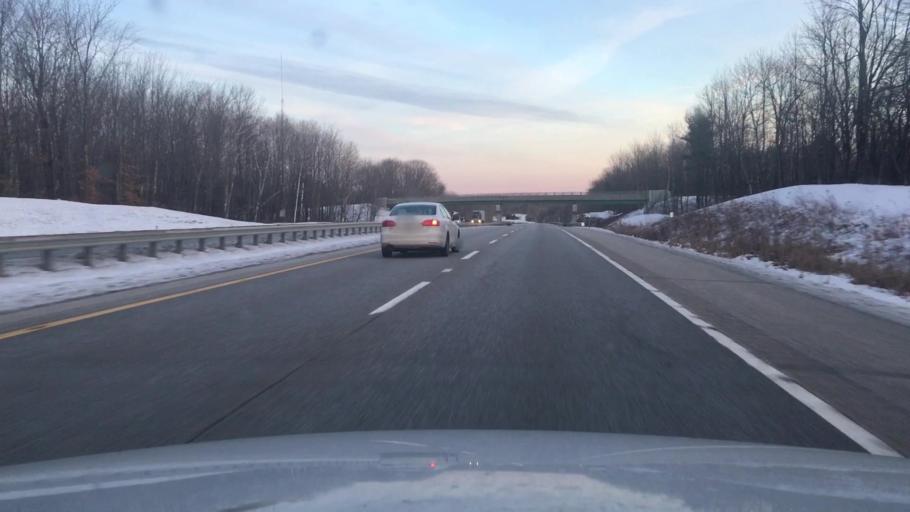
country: US
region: Maine
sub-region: Androscoggin County
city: Sabattus
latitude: 44.1250
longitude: -69.9831
